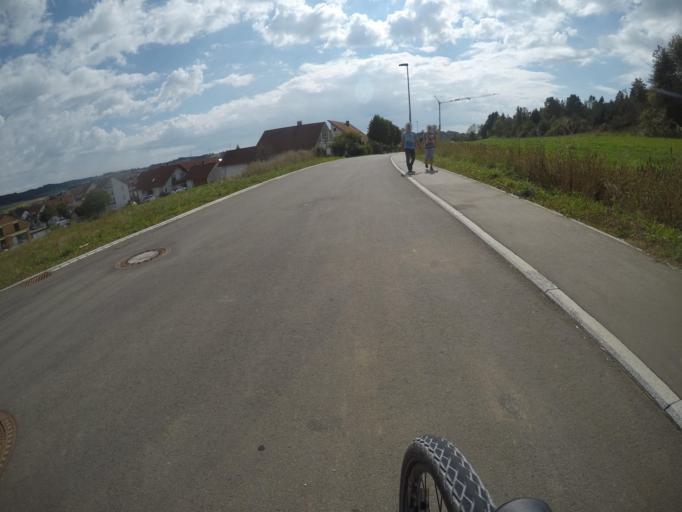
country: DE
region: Baden-Wuerttemberg
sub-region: Tuebingen Region
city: Munsingen
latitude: 48.4192
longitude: 9.4986
